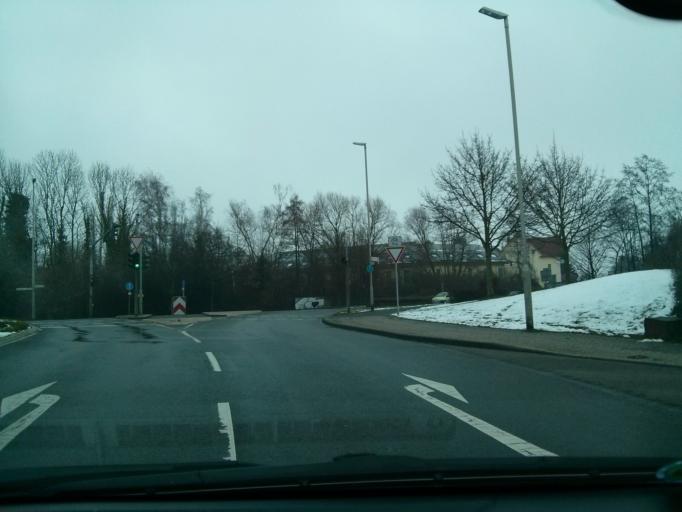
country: DE
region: North Rhine-Westphalia
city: Meckenheim
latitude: 50.6279
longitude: 7.0219
